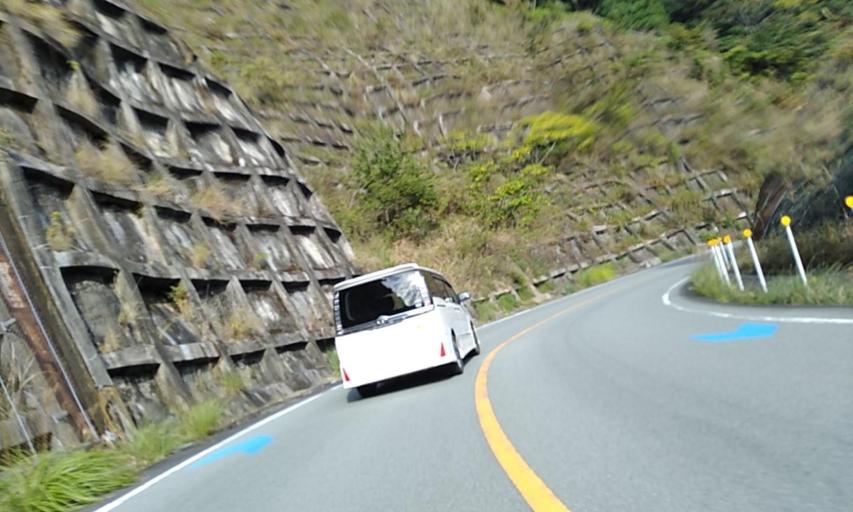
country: JP
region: Mie
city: Owase
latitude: 34.2185
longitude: 136.3836
